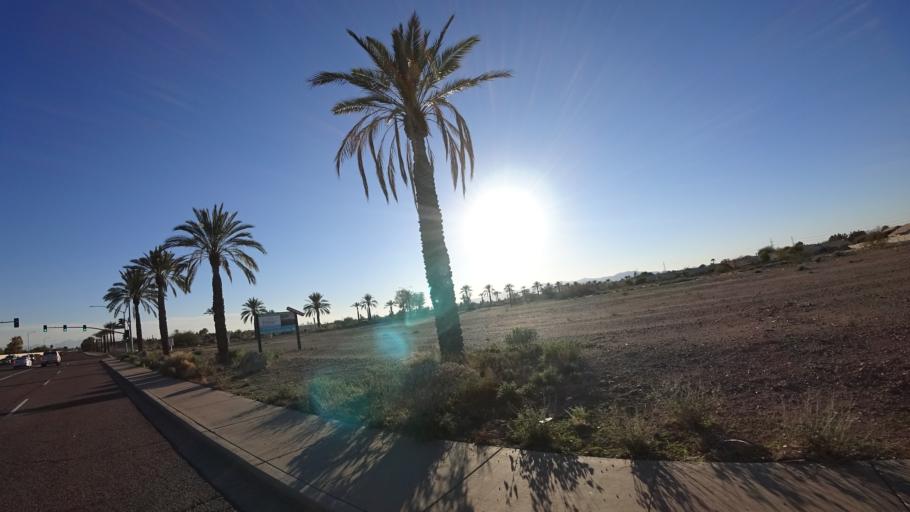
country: US
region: Arizona
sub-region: Maricopa County
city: Sun City West
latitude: 33.6680
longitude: -112.2901
